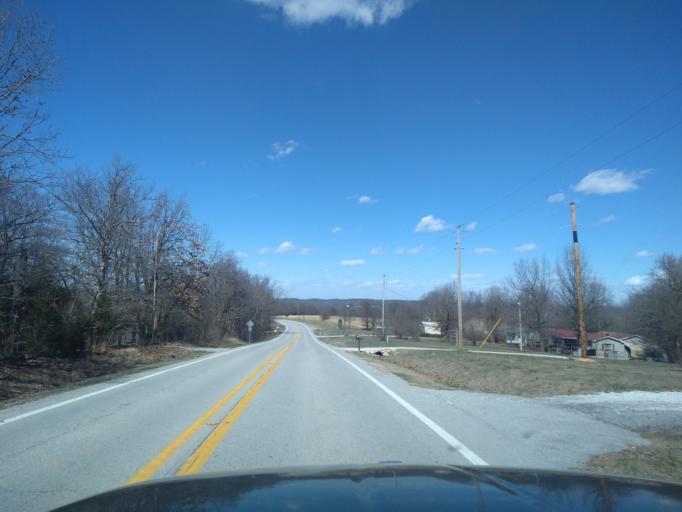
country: US
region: Arkansas
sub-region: Washington County
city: Farmington
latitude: 36.0932
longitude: -94.3316
